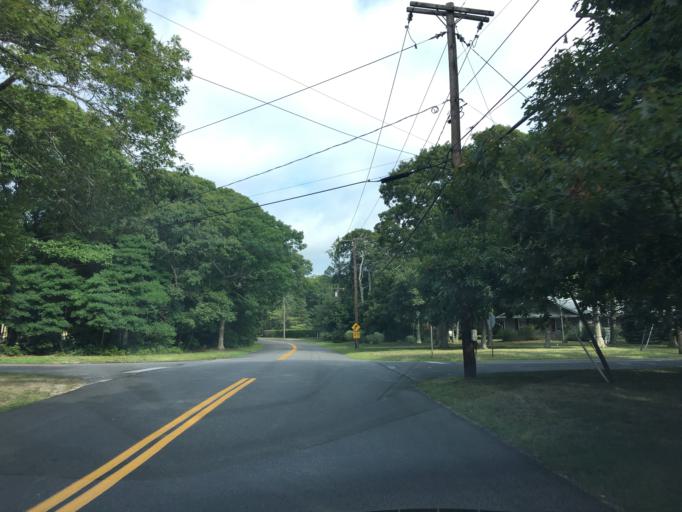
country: US
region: New York
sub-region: Suffolk County
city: Shelter Island
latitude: 41.0494
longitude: -72.3609
